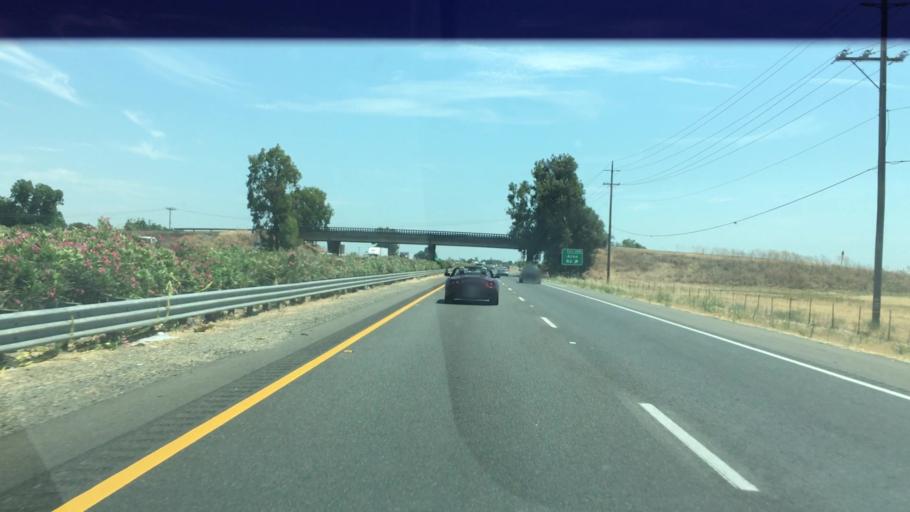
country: US
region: California
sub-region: Sacramento County
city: Galt
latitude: 38.3263
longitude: -121.3279
